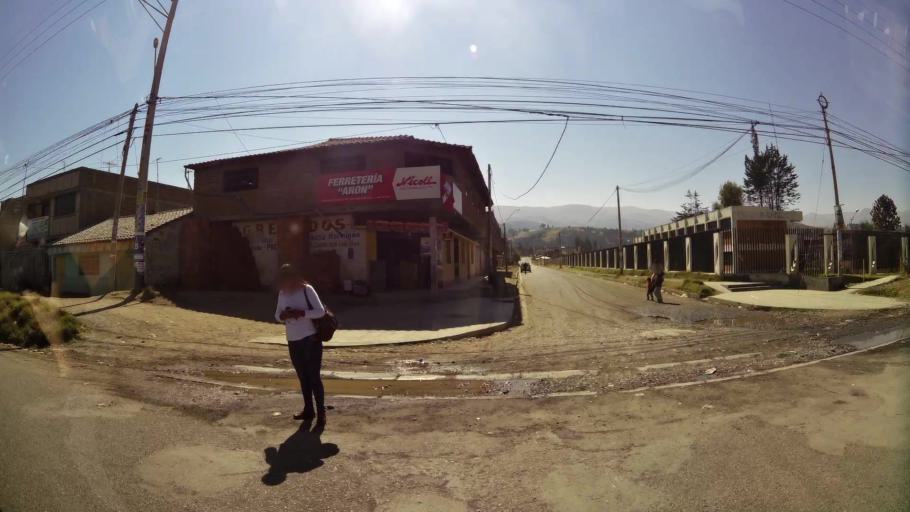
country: PE
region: Junin
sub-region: Provincia de Huancayo
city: San Agustin
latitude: -11.9978
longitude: -75.2538
